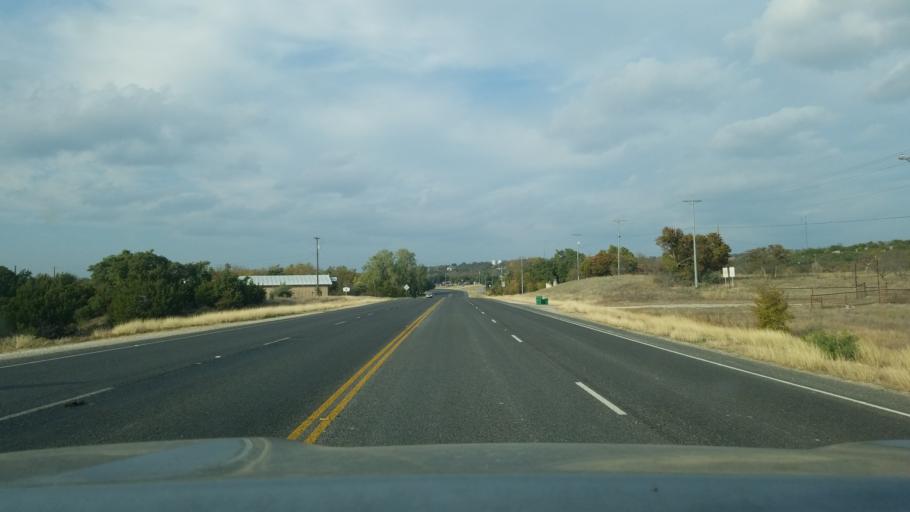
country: US
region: Texas
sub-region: Mills County
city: Goldthwaite
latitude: 31.4408
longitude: -98.5681
